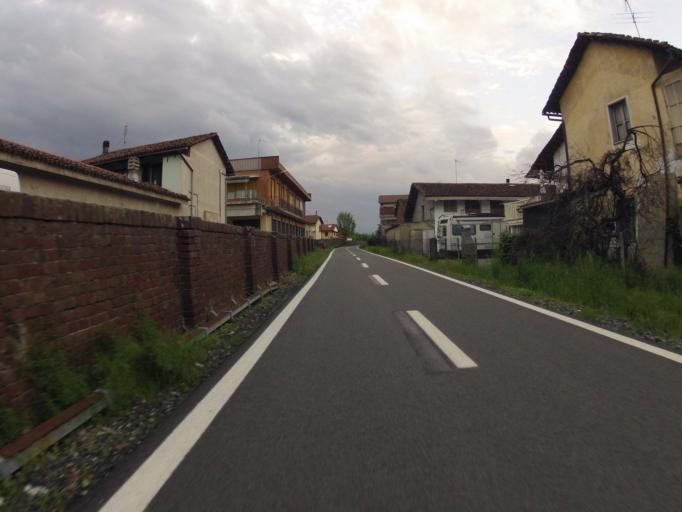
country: IT
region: Piedmont
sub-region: Provincia di Torino
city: Vigone
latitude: 44.8433
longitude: 7.4905
